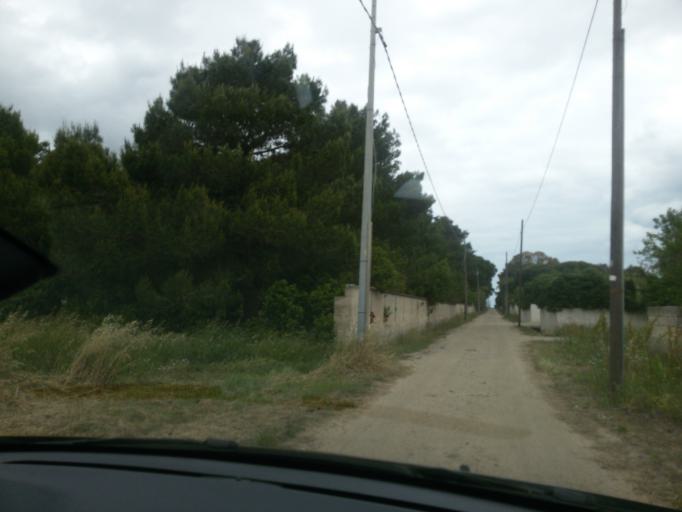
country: IT
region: Apulia
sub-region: Provincia di Brindisi
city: Brindisi
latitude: 40.6339
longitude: 17.8973
